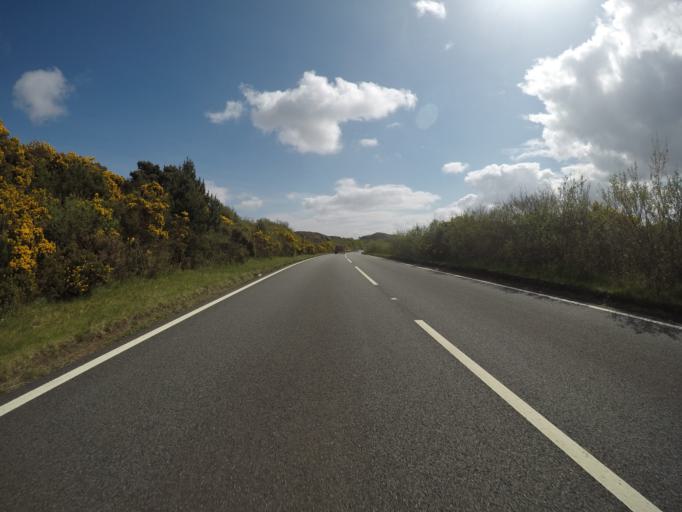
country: GB
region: Scotland
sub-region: Highland
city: Portree
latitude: 57.5234
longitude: -6.3432
